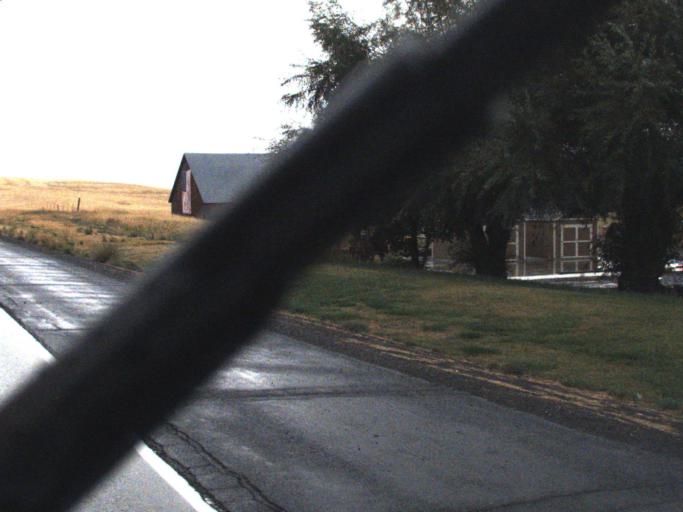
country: US
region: Washington
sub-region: Whitman County
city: Colfax
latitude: 47.1795
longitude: -117.3780
